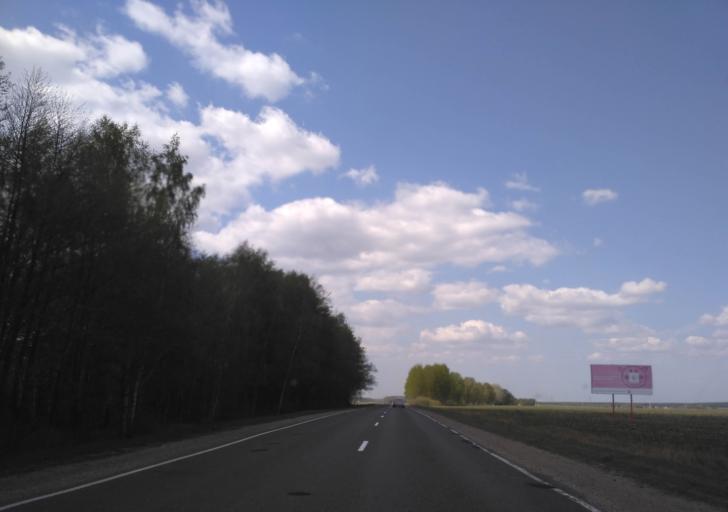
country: BY
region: Minsk
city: Vilyeyka
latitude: 54.5100
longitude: 27.0562
